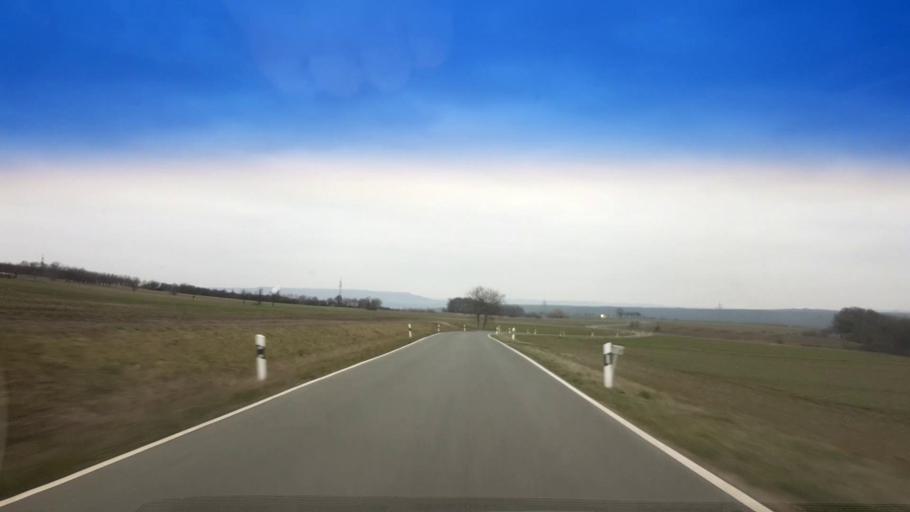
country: DE
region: Bavaria
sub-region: Upper Franconia
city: Hallerndorf
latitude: 49.7671
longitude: 10.9545
